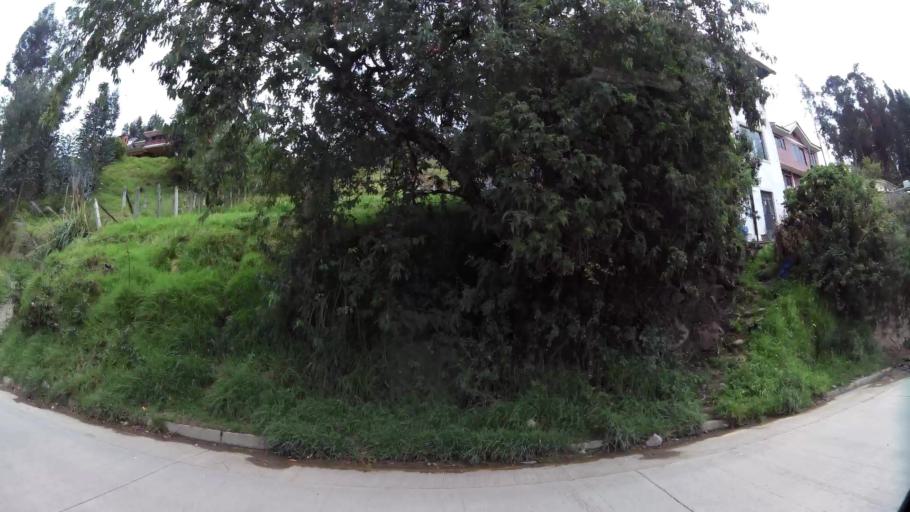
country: EC
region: Azuay
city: Cuenca
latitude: -2.8719
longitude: -79.0766
